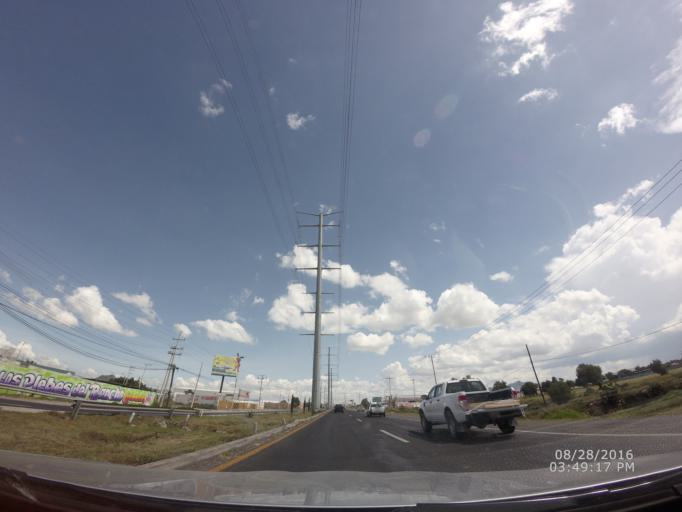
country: MX
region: Hidalgo
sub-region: Mineral de la Reforma
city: Los Tuzos
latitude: 20.0458
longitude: -98.7362
